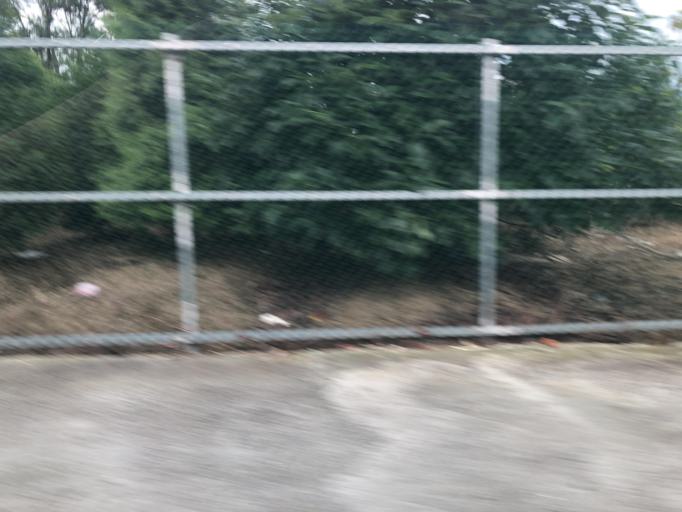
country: TW
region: Taiwan
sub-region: Taoyuan
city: Taoyuan
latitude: 24.9226
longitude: 121.3647
